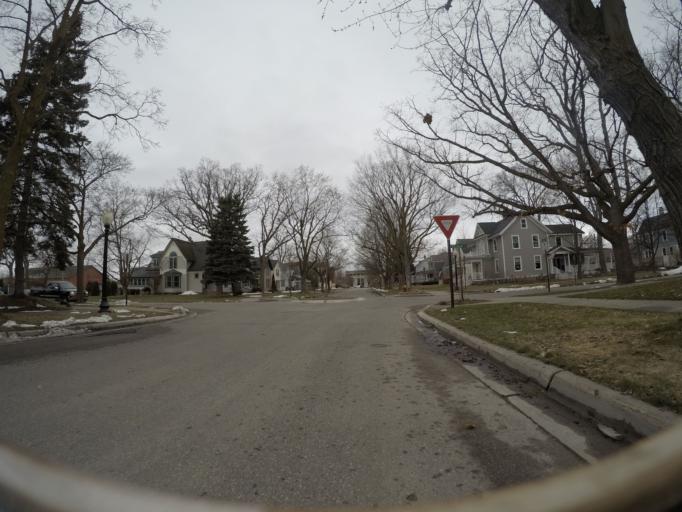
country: US
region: Michigan
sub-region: Grand Traverse County
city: Traverse City
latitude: 44.7606
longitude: -85.6132
